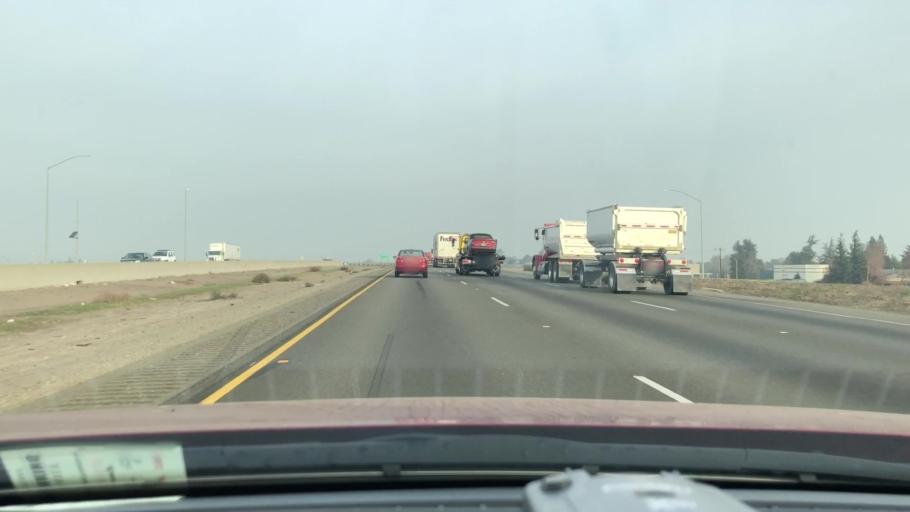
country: US
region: California
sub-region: San Joaquin County
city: French Camp
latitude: 37.8953
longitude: -121.2832
